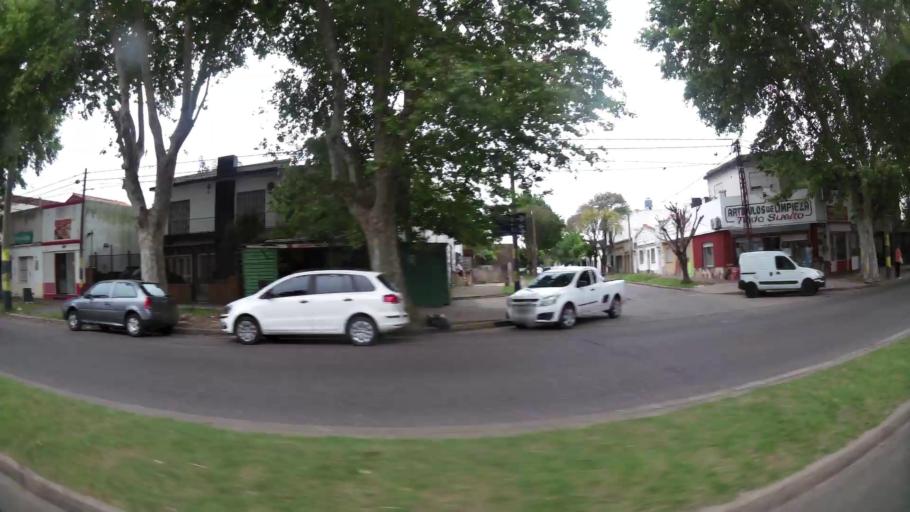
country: AR
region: Santa Fe
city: Granadero Baigorria
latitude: -32.8831
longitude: -60.6958
